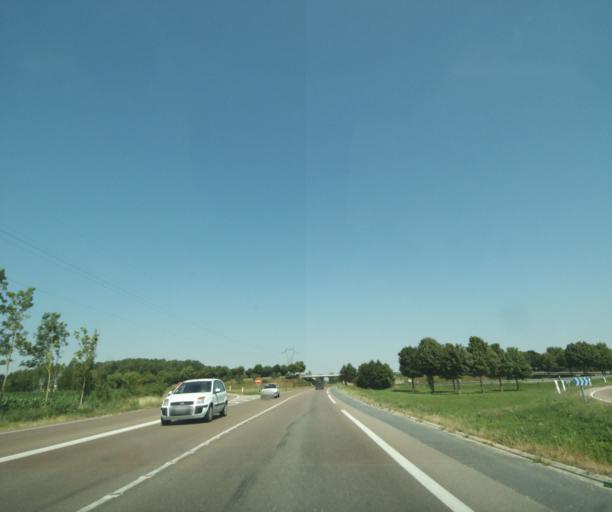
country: FR
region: Champagne-Ardenne
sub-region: Departement de la Marne
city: Frignicourt
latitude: 48.7125
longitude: 4.6390
